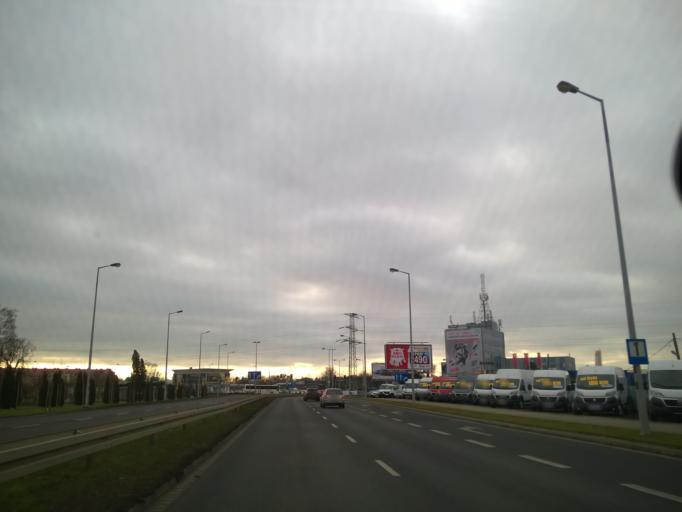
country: PL
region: Lower Silesian Voivodeship
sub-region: Powiat wroclawski
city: Bielany Wroclawskie
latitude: 51.0651
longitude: 17.0024
